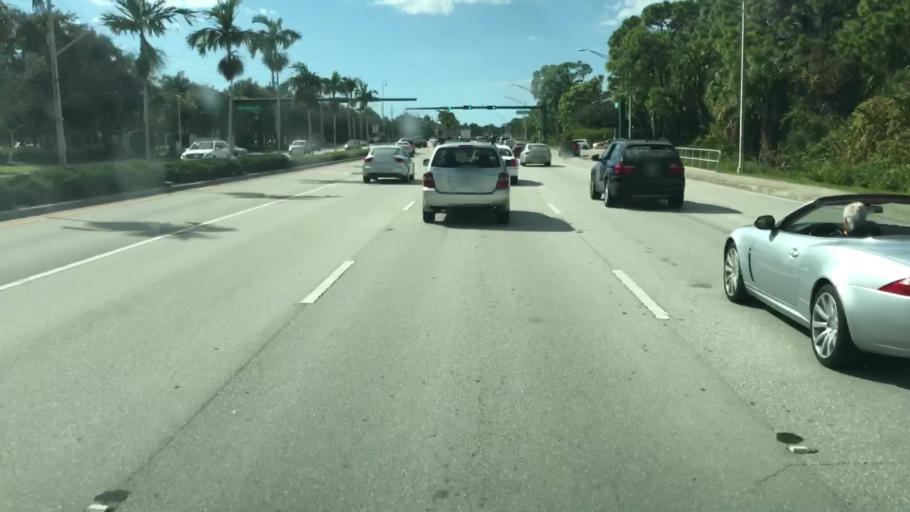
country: US
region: Florida
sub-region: Collier County
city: Naples Park
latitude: 26.2723
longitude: -81.7945
